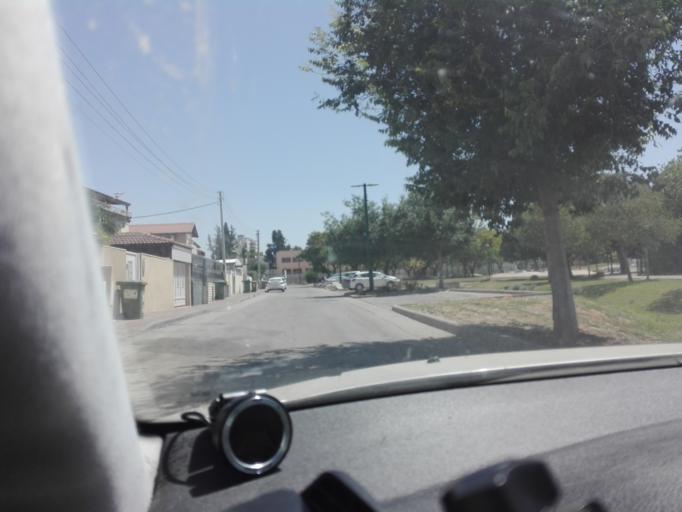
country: IL
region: Central District
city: Bene 'Ayish
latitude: 31.7329
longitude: 34.7453
